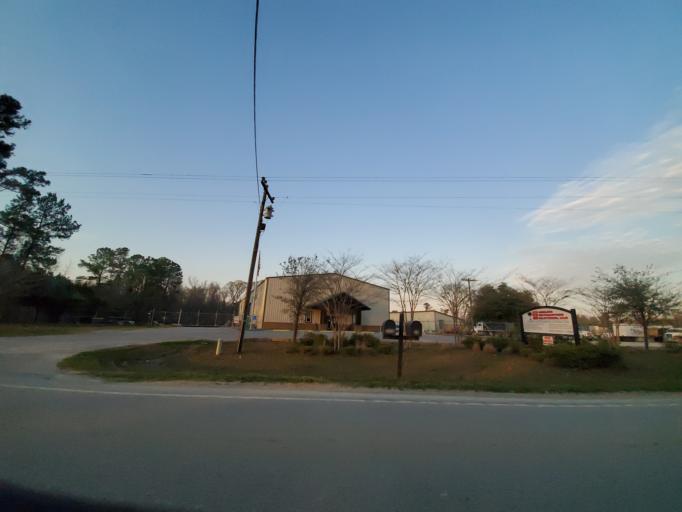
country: US
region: South Carolina
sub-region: Dorchester County
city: Ridgeville
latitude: 33.0078
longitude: -80.3305
